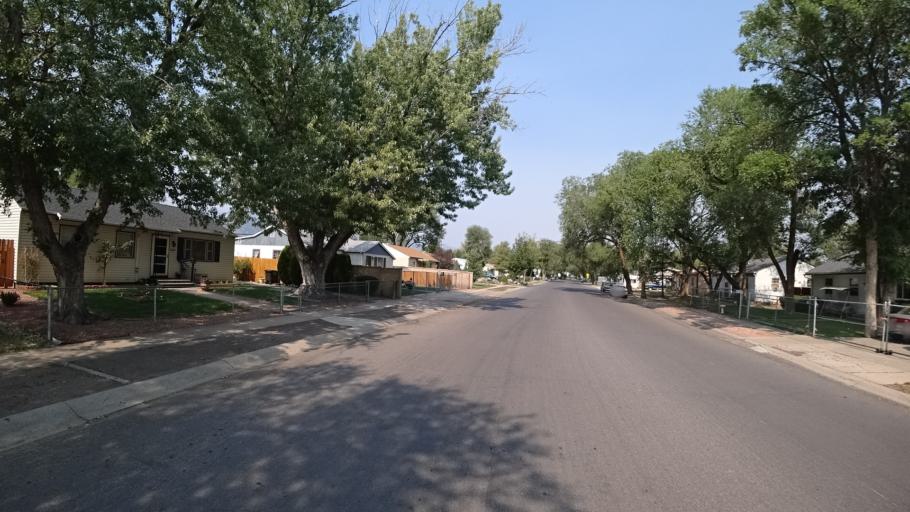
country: US
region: Colorado
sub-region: El Paso County
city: Colorado Springs
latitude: 38.8034
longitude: -104.8150
